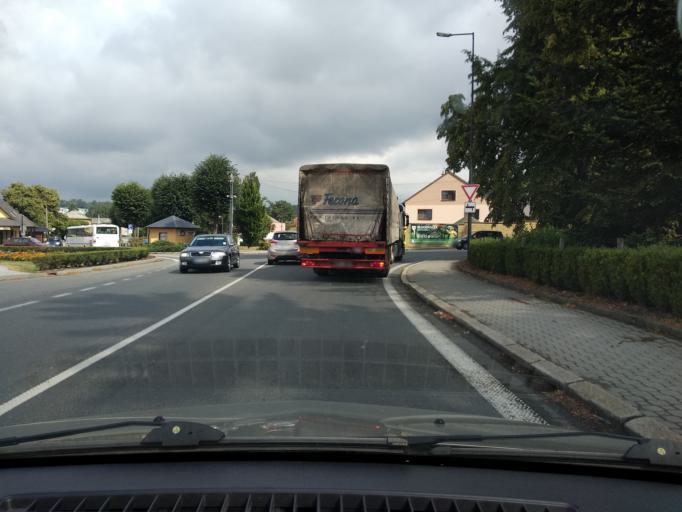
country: CZ
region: Olomoucky
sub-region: Okres Sumperk
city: Bludov
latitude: 49.9405
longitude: 16.9281
